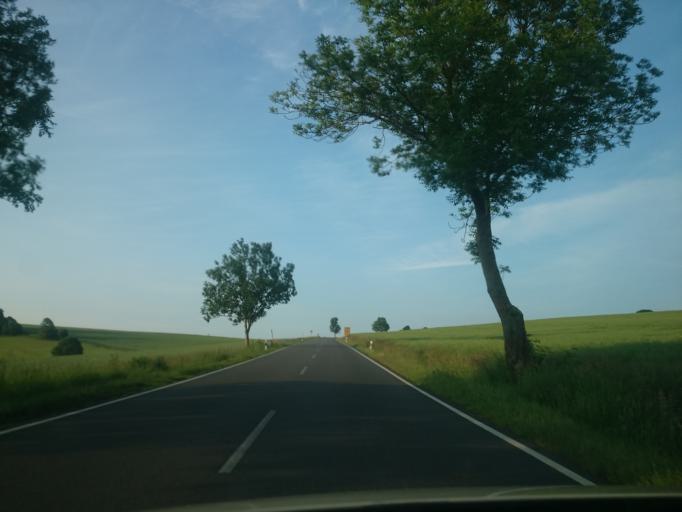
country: DE
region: Saxony
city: Grosshartmannsdorf
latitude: 50.7813
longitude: 13.3220
